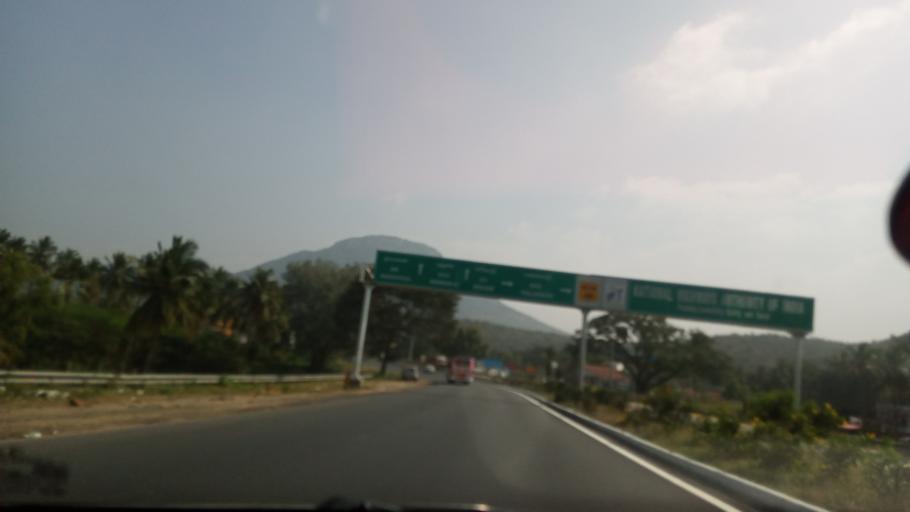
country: IN
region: Tamil Nadu
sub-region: Salem
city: Omalur
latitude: 11.9386
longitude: 78.0524
